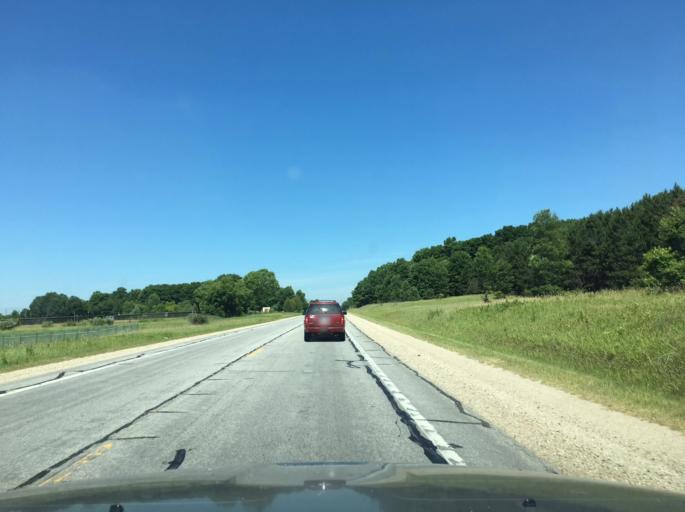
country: US
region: Michigan
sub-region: Osceola County
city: Reed City
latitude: 43.8749
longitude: -85.4939
